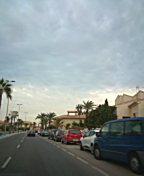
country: ES
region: Murcia
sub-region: Murcia
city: La Manga del Mar Menor
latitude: 37.7042
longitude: -0.7418
